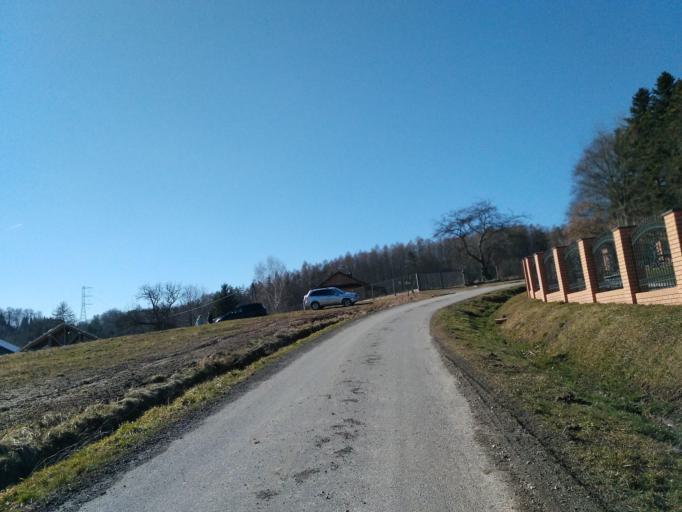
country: PL
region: Subcarpathian Voivodeship
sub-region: Powiat strzyzowski
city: Babica
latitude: 49.9517
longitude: 21.8846
